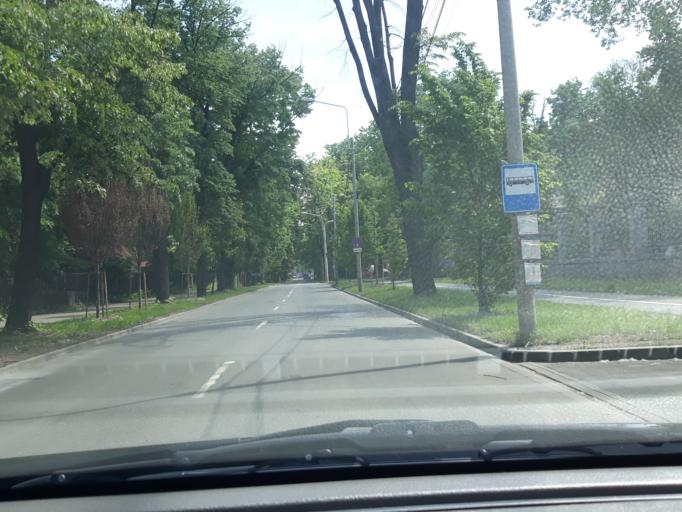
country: RO
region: Bihor
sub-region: Comuna Biharea
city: Oradea
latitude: 47.0505
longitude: 21.9214
